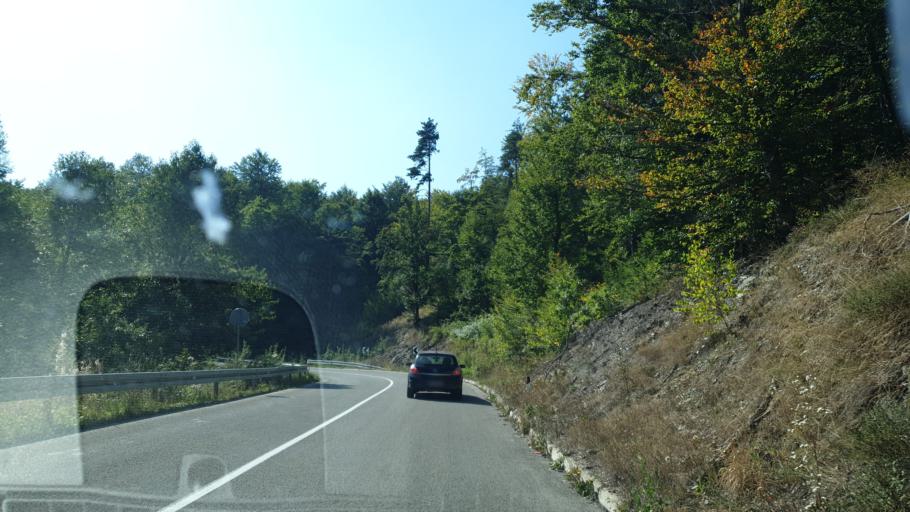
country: RS
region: Central Serbia
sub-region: Zlatiborski Okrug
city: Cajetina
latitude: 43.7176
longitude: 19.7816
